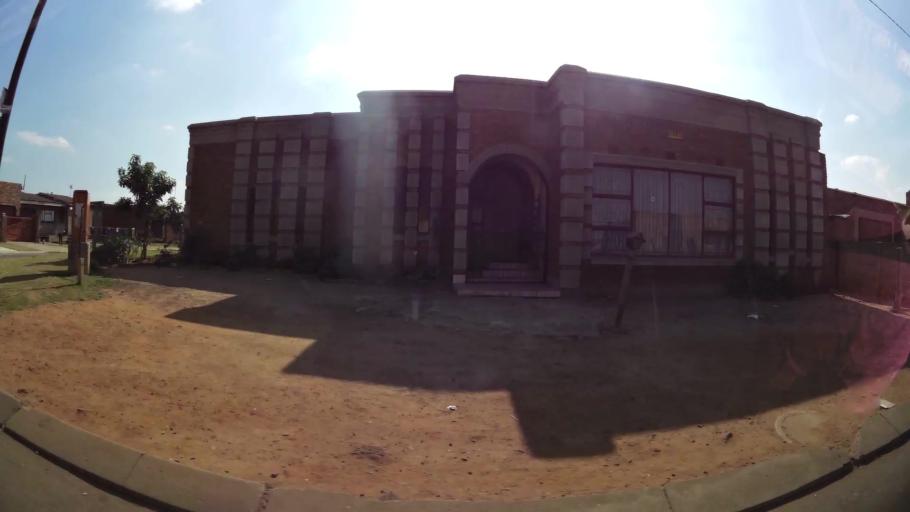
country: ZA
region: Gauteng
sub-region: Ekurhuleni Metropolitan Municipality
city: Benoni
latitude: -26.1411
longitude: 28.4130
